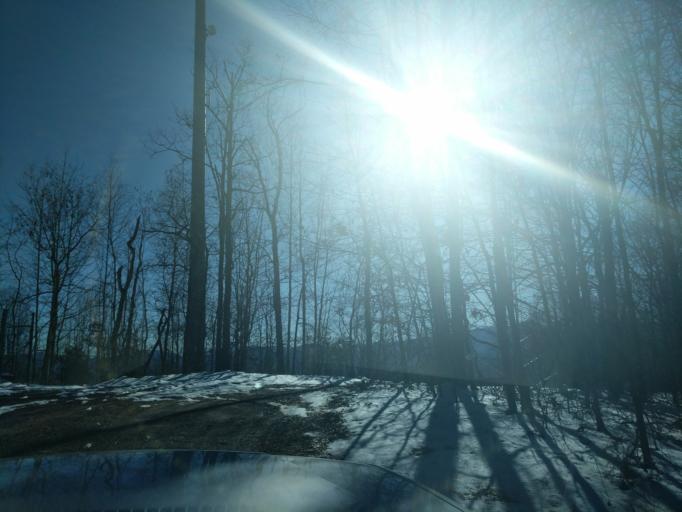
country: US
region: Georgia
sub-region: Towns County
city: Hiawassee
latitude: 34.9544
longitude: -83.7297
